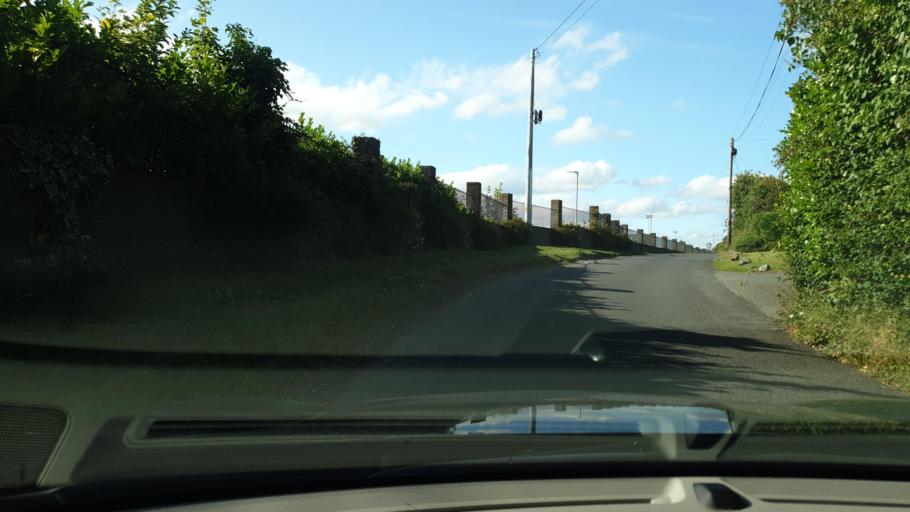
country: IE
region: Leinster
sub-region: An Mhi
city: Ashbourne
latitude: 53.5084
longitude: -6.3846
